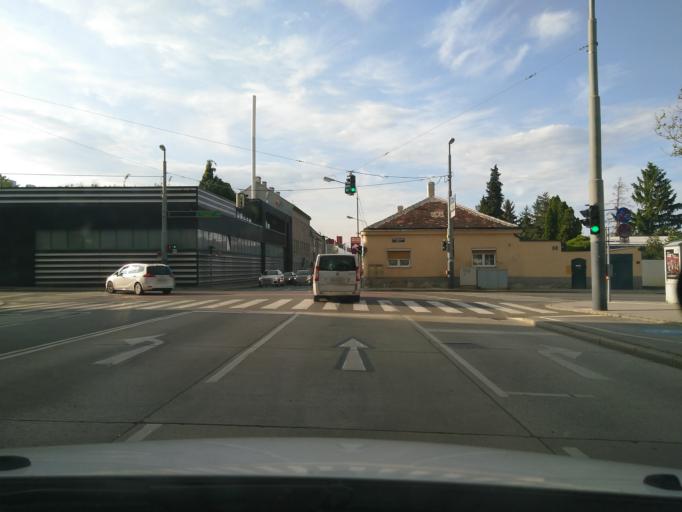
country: AT
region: Lower Austria
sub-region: Politischer Bezirk Modling
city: Brunn am Gebirge
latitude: 48.1409
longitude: 16.2981
